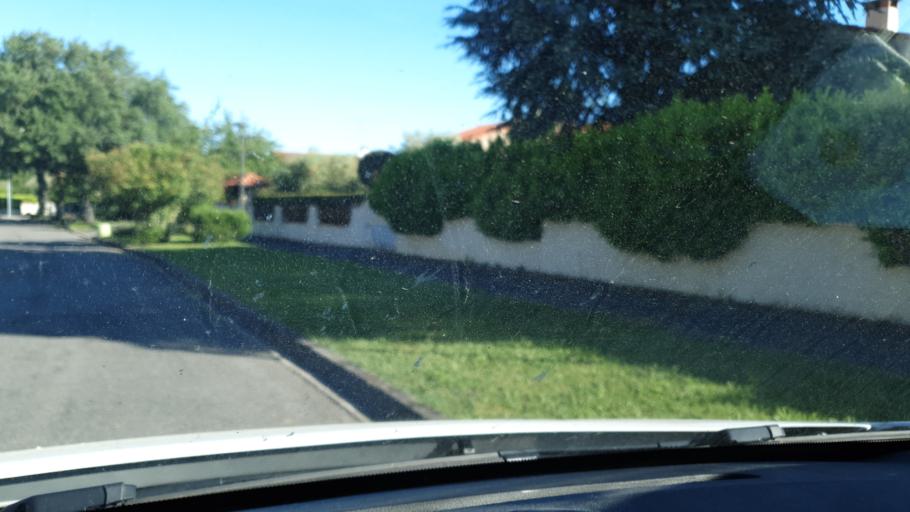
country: FR
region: Midi-Pyrenees
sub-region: Departement de la Haute-Garonne
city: Saint-Orens-de-Gameville
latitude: 43.5577
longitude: 1.5176
